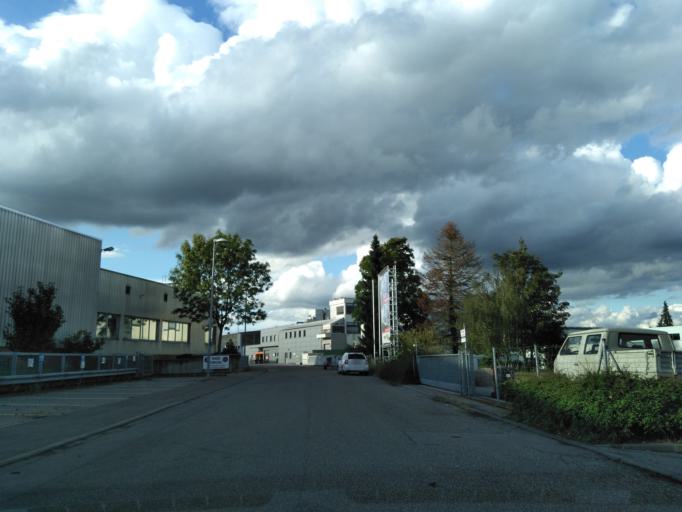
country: DE
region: Baden-Wuerttemberg
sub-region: Regierungsbezirk Stuttgart
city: Markgroningen
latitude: 48.9344
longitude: 9.0646
